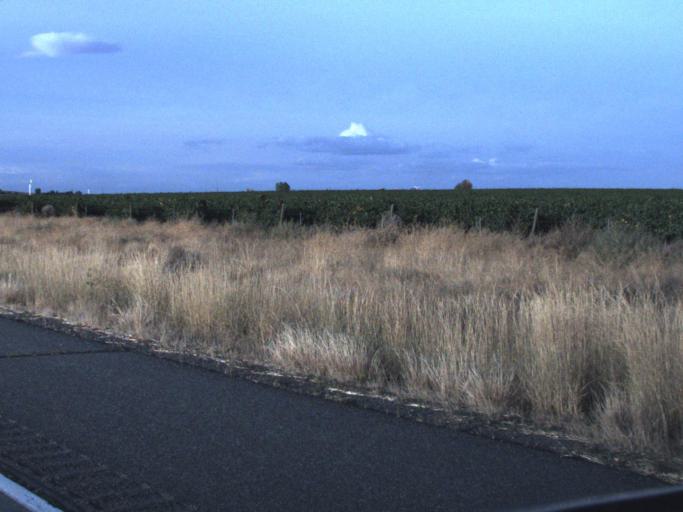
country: US
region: Washington
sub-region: Benton County
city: West Richland
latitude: 46.2341
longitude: -119.3568
